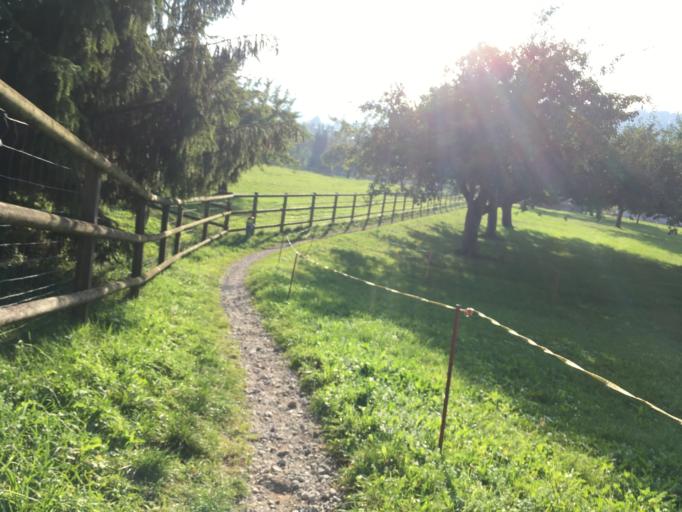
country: CH
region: Saint Gallen
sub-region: Wahlkreis Toggenburg
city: Buetschwil
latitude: 47.3538
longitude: 9.0855
